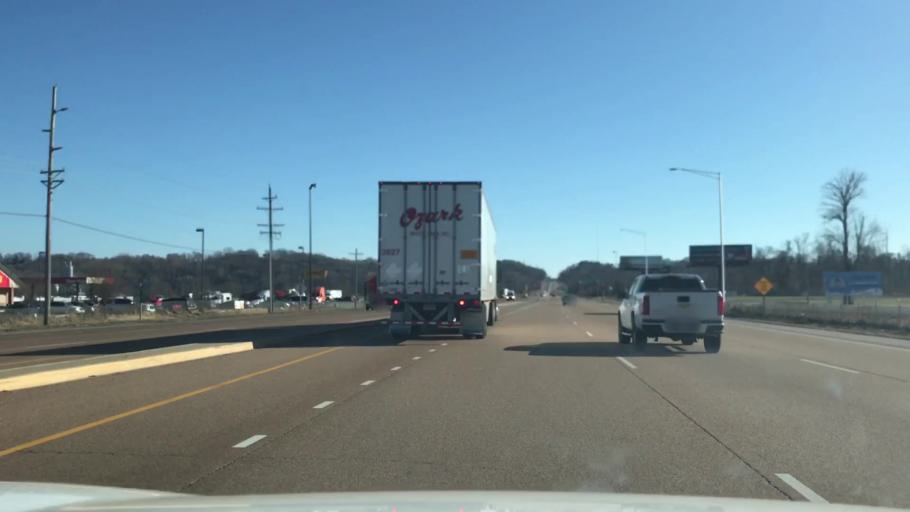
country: US
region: Illinois
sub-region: Saint Clair County
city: Alorton
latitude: 38.5761
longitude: -90.1008
